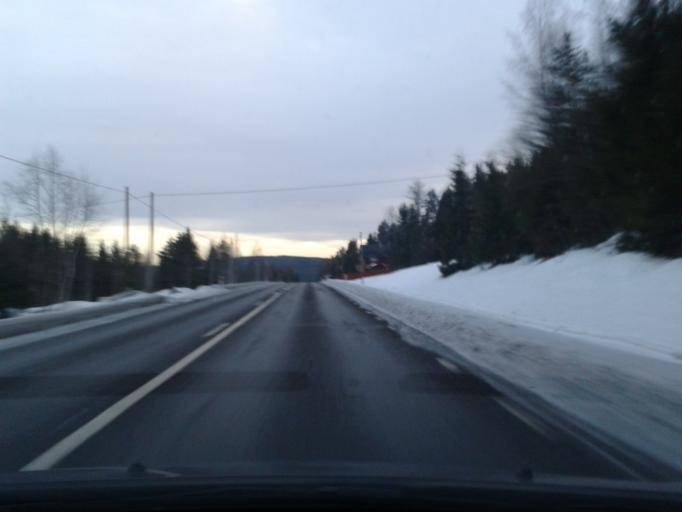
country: SE
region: Vaesternorrland
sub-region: Kramfors Kommun
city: Bollstabruk
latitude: 63.0860
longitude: 17.5335
